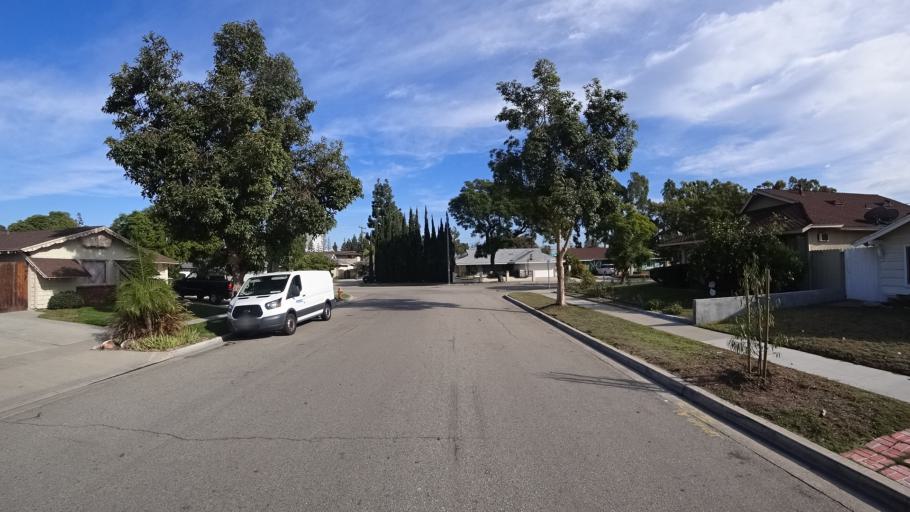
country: US
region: California
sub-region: Orange County
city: Garden Grove
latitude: 33.7785
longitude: -117.9006
